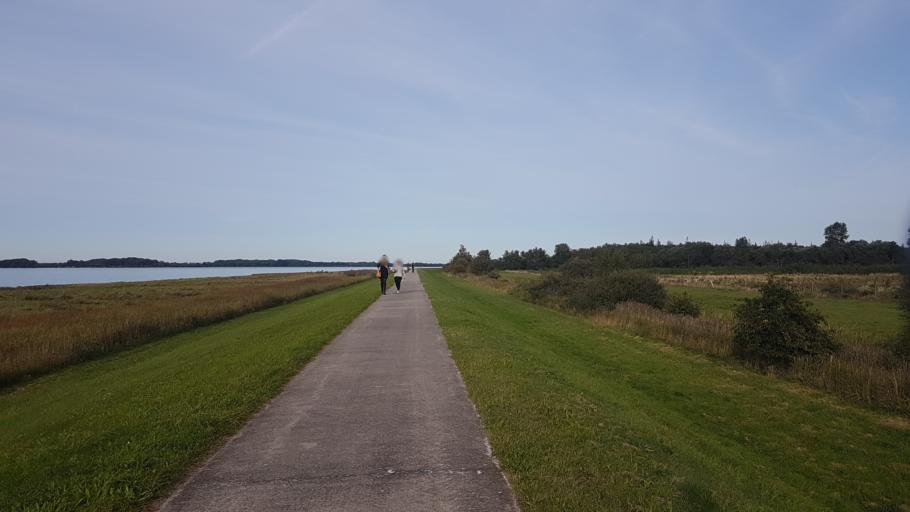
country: DE
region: Mecklenburg-Vorpommern
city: Hiddensee
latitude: 54.4851
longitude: 13.1561
